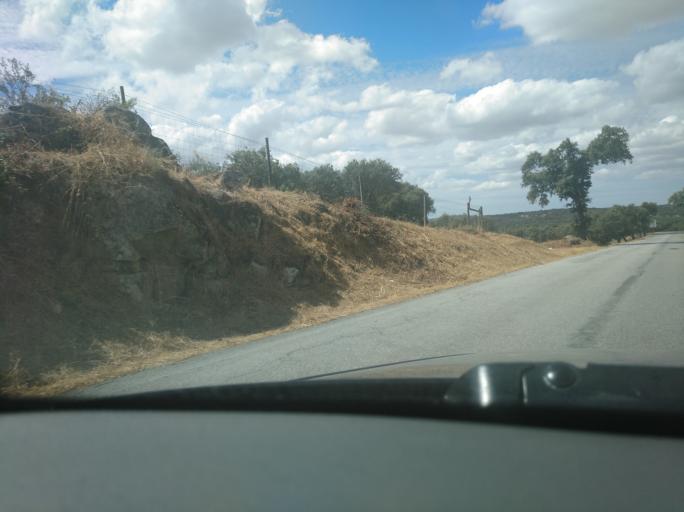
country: PT
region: Portalegre
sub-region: Arronches
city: Arronches
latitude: 39.0586
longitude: -7.4358
